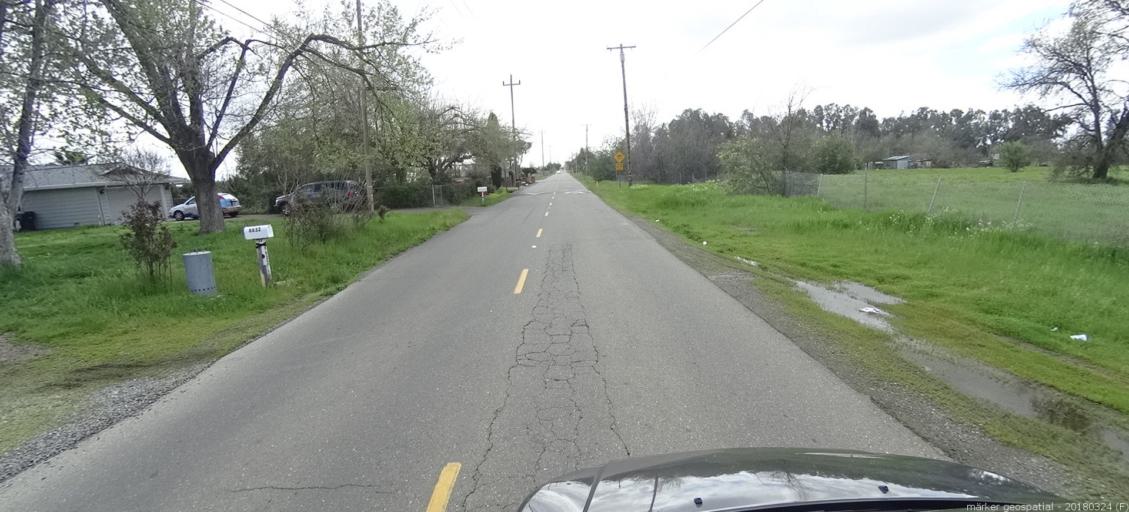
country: US
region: California
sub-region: Sacramento County
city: North Highlands
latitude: 38.6884
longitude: -121.3875
